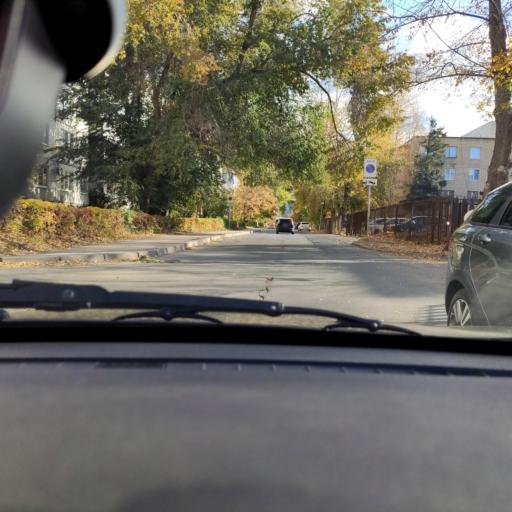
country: RU
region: Samara
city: Tol'yatti
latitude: 53.5324
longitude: 49.2636
